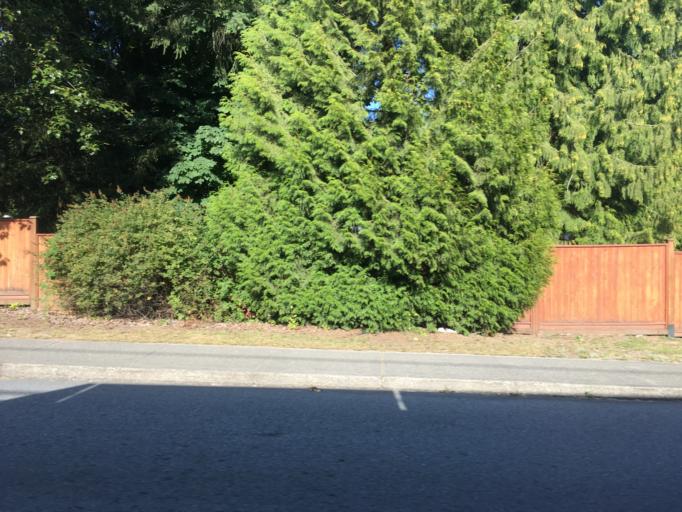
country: CA
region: British Columbia
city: Port Moody
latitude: 49.2489
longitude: -122.8245
